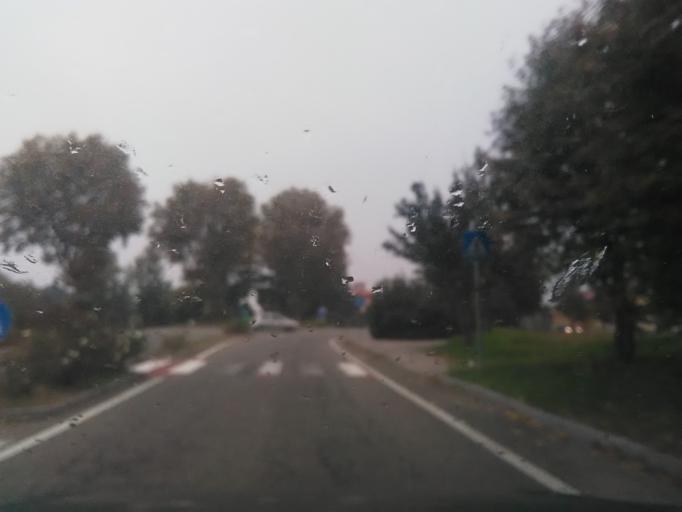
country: IT
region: Piedmont
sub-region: Provincia di Biella
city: Cavaglia
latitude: 45.4085
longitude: 8.0958
